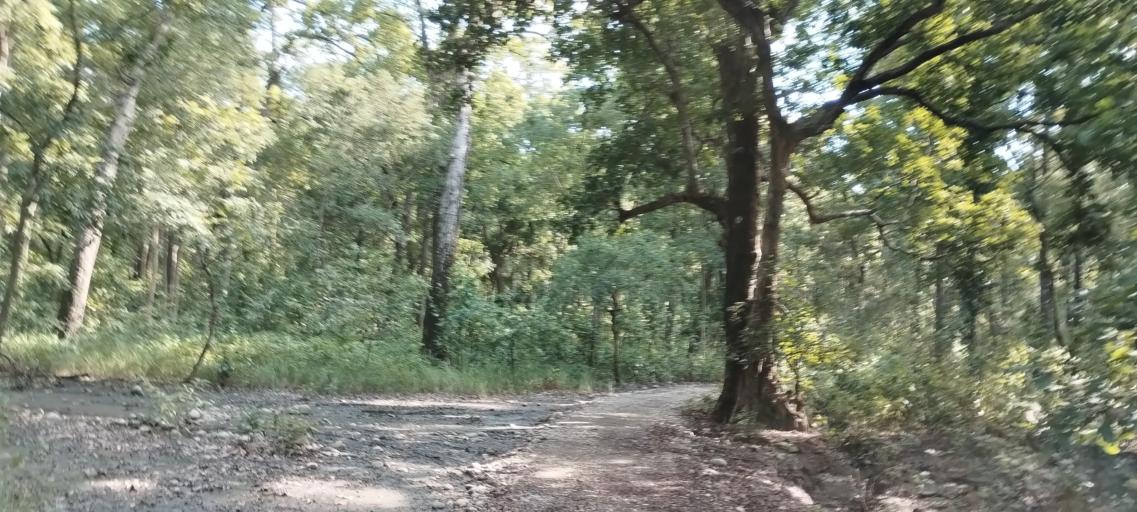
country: NP
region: Far Western
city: Tikapur
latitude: 28.5569
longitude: 81.2657
